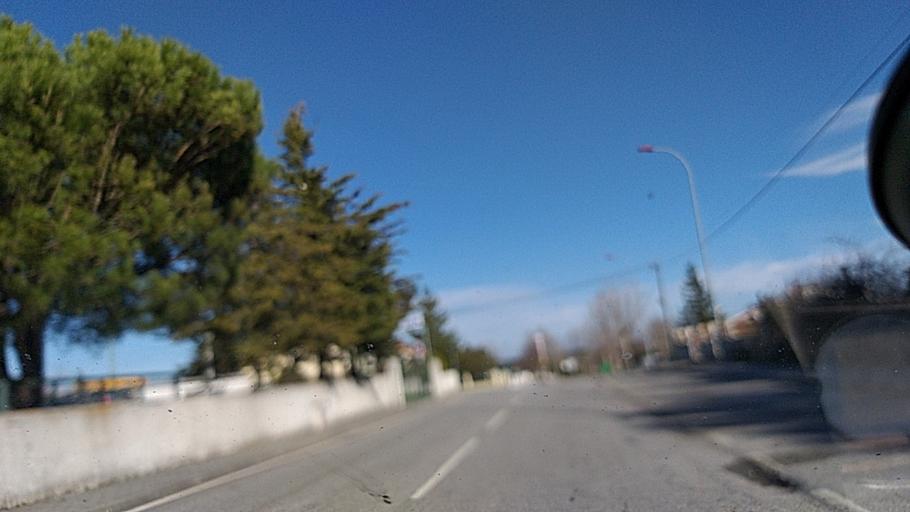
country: ES
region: Castille and Leon
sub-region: Provincia de Salamanca
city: Fuentes de Onoro
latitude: 40.6176
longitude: -6.8443
